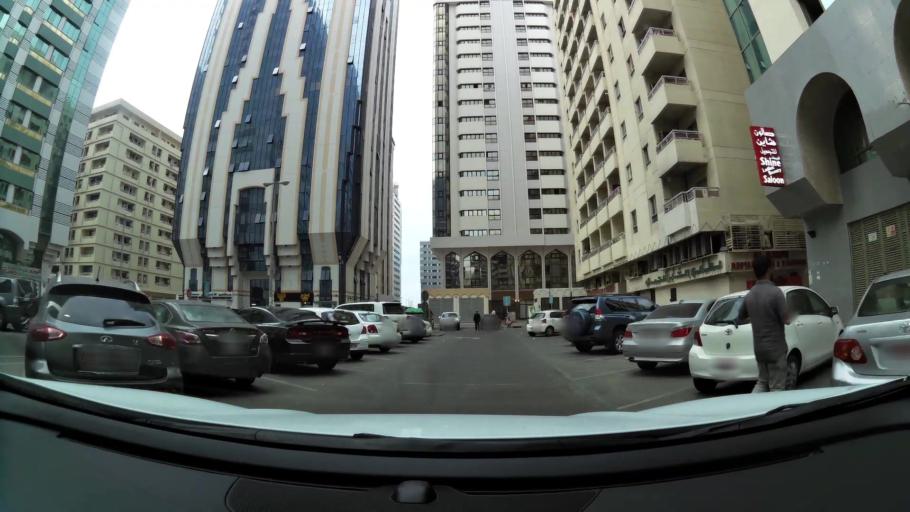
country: AE
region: Abu Dhabi
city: Abu Dhabi
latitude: 24.5005
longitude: 54.3756
